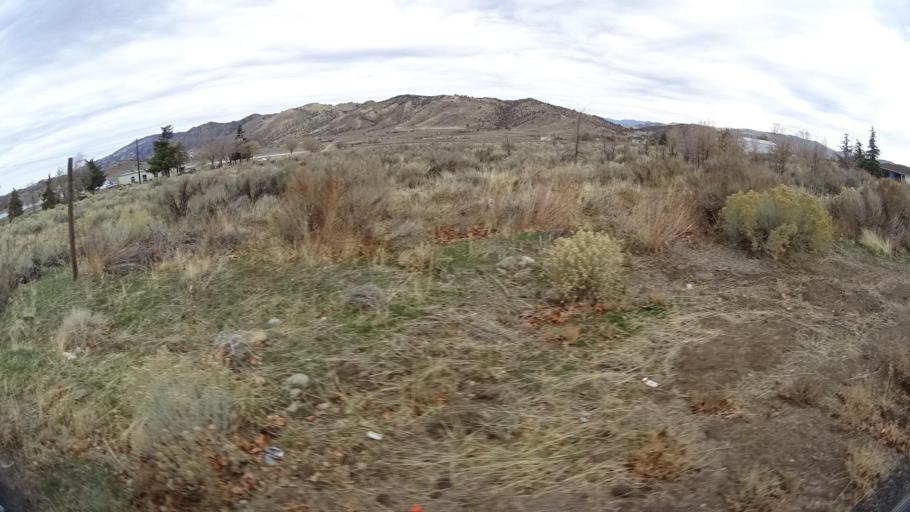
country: US
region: California
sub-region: Kern County
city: Golden Hills
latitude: 35.1020
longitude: -118.5357
